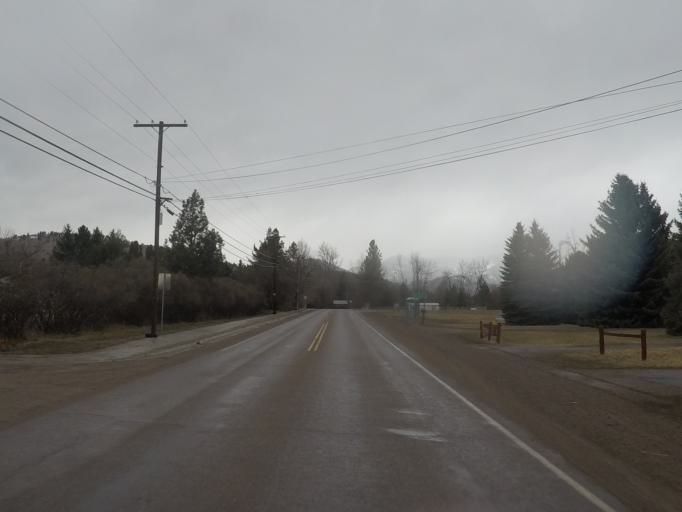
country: US
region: Montana
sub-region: Missoula County
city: East Missoula
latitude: 46.8985
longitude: -113.9656
